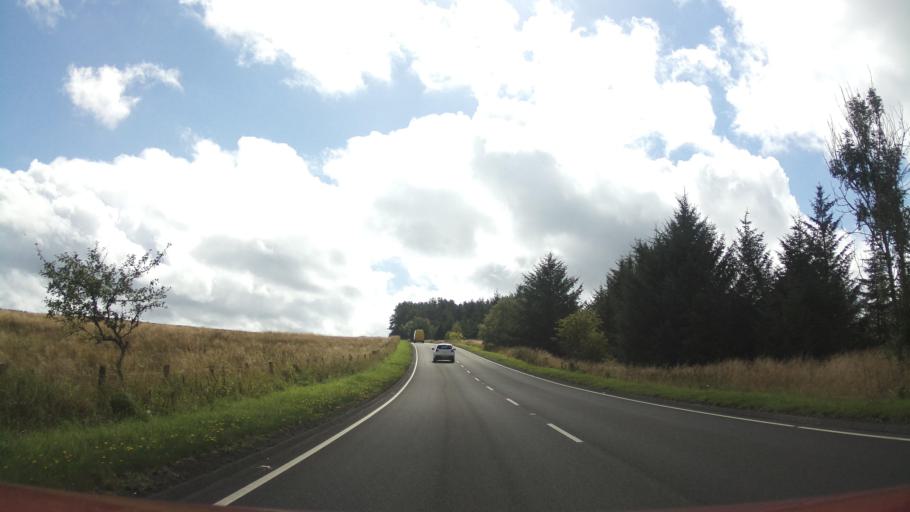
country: GB
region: Scotland
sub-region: The Scottish Borders
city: Jedburgh
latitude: 55.3788
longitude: -2.4957
